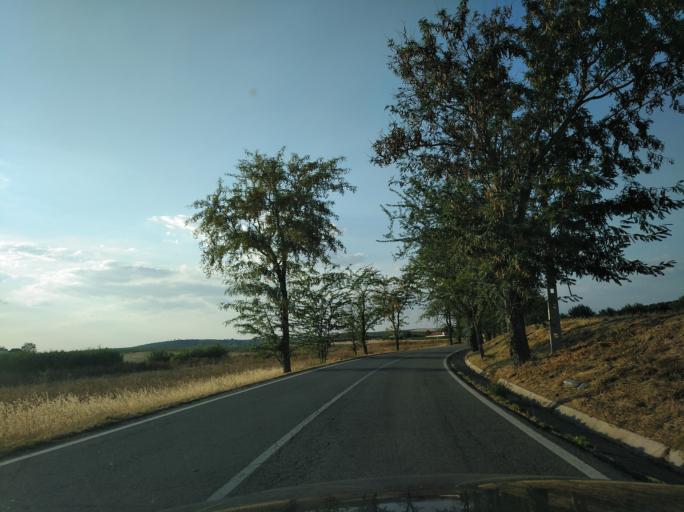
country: PT
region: Portalegre
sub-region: Campo Maior
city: Campo Maior
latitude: 38.9853
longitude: -7.0678
